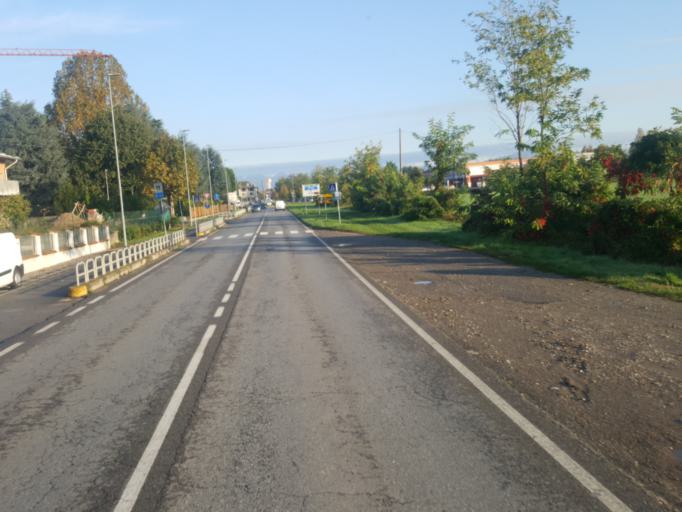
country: IT
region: Lombardy
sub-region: Provincia di Bergamo
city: Cologno al Serio
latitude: 45.5707
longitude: 9.7087
